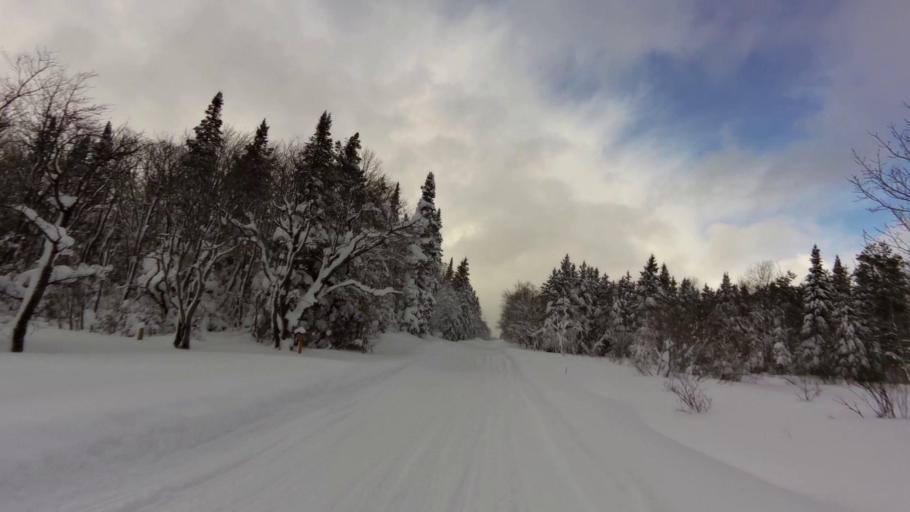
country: US
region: New York
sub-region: Lewis County
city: Lowville
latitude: 43.7367
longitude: -75.6714
